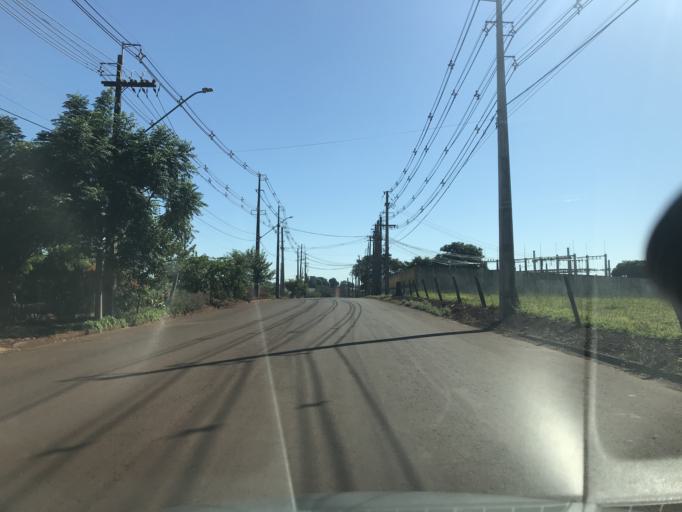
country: BR
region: Parana
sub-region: Palotina
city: Palotina
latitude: -24.2754
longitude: -53.8254
